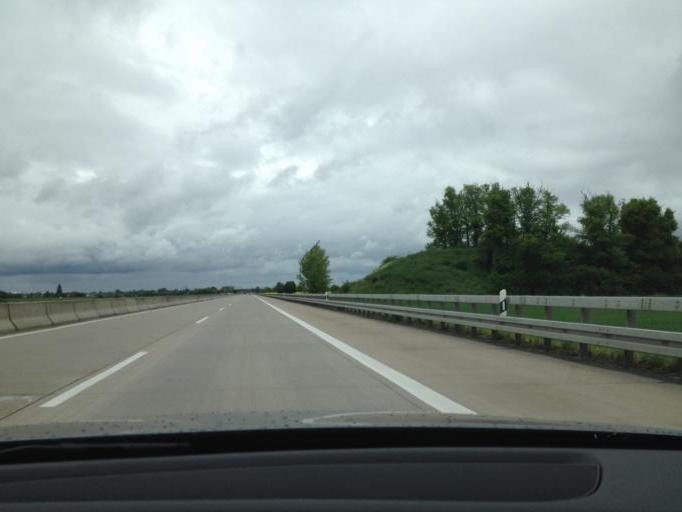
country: DE
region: Baden-Wuerttemberg
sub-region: Karlsruhe Region
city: Edingen-Neckarhausen
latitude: 49.4304
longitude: 8.6125
